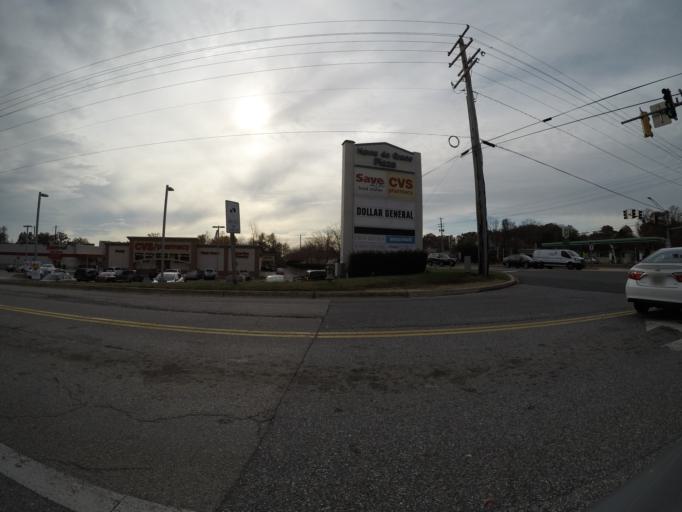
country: US
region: Maryland
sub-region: Harford County
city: Havre de Grace
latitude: 39.5462
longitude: -76.1063
